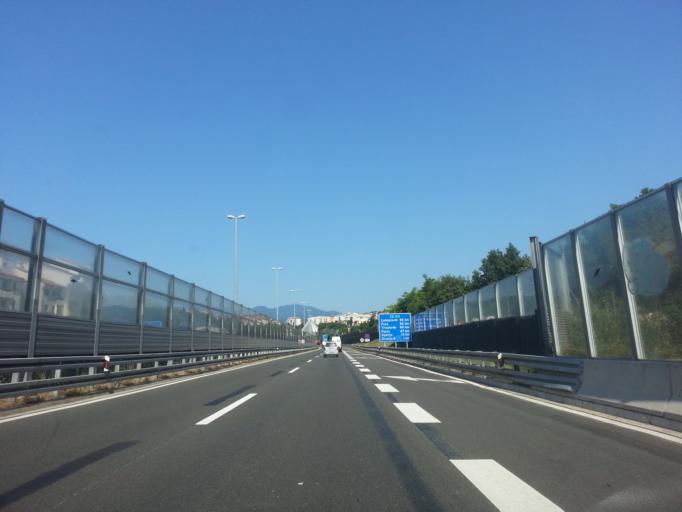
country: HR
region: Primorsko-Goranska
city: Rijeka
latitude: 45.3452
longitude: 14.3963
